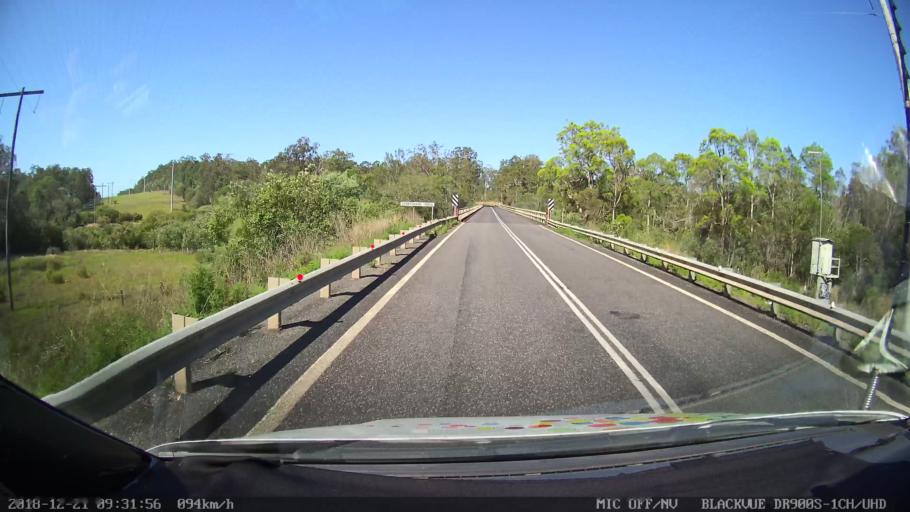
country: AU
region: New South Wales
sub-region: Clarence Valley
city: Maclean
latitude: -29.4651
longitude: 152.9832
